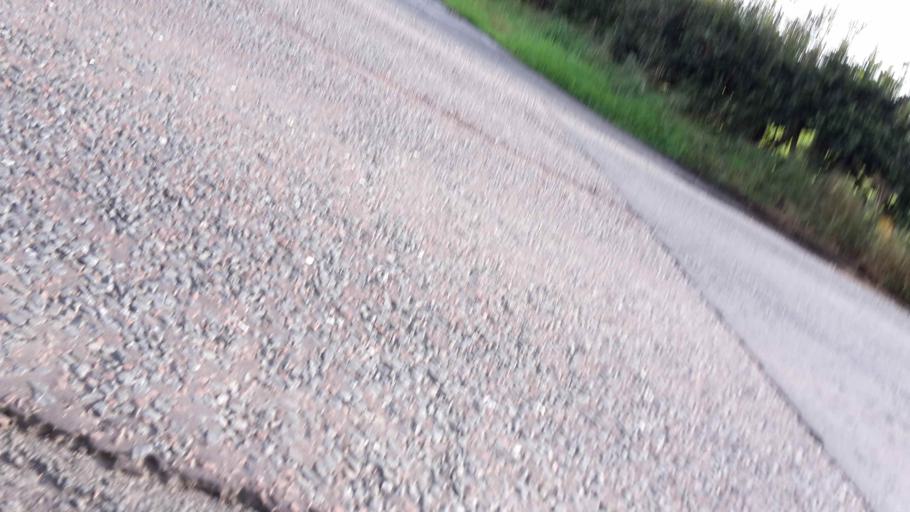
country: GB
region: Scotland
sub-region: South Lanarkshire
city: Carluke
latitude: 55.7172
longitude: -3.8261
